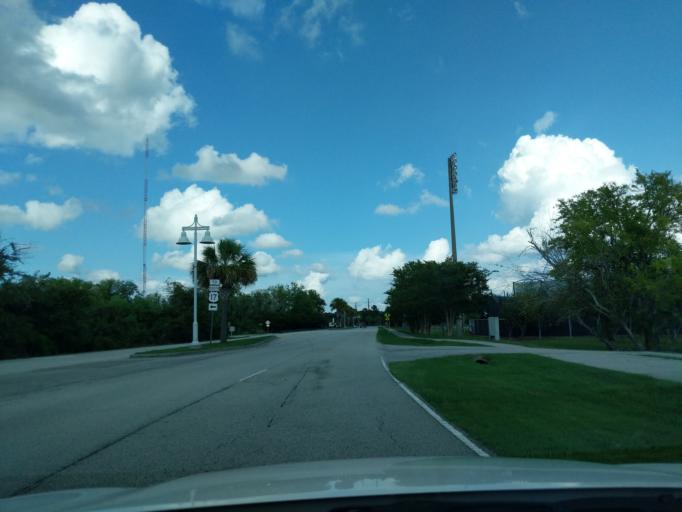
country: US
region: South Carolina
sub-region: Charleston County
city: Charleston
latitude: 32.7964
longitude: -79.9029
